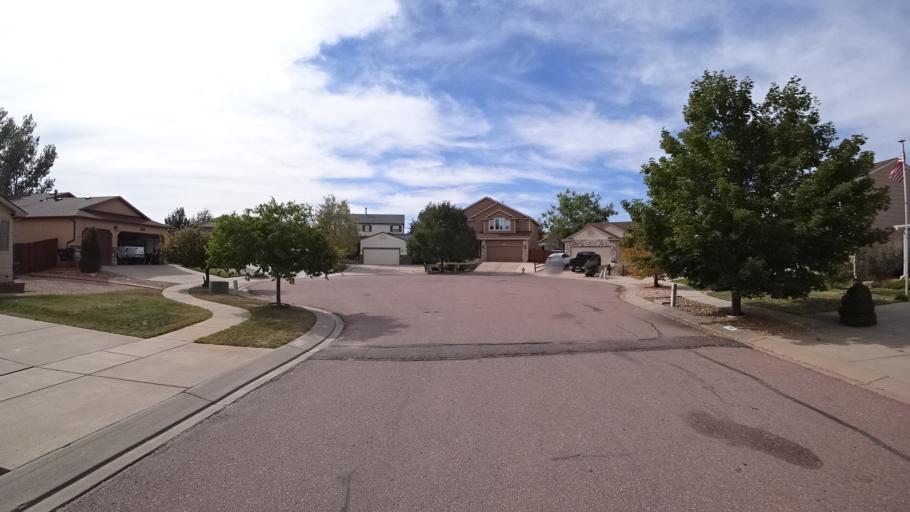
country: US
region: Colorado
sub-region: El Paso County
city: Cimarron Hills
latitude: 38.9022
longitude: -104.6883
